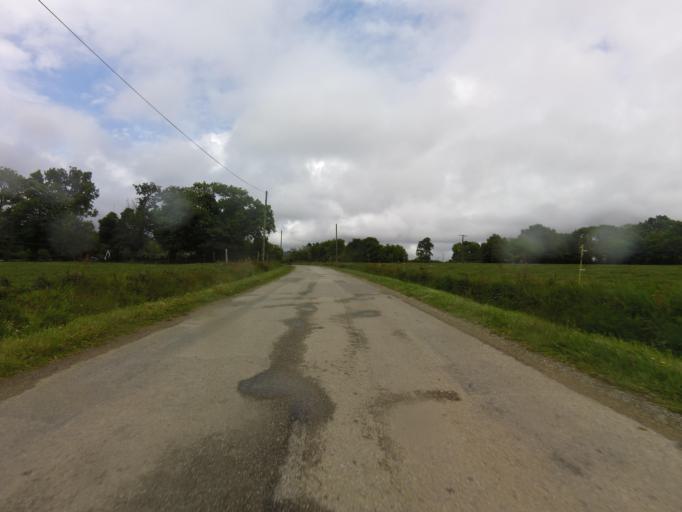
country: FR
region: Brittany
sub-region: Departement du Morbihan
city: Baden
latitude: 47.6318
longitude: -2.9156
